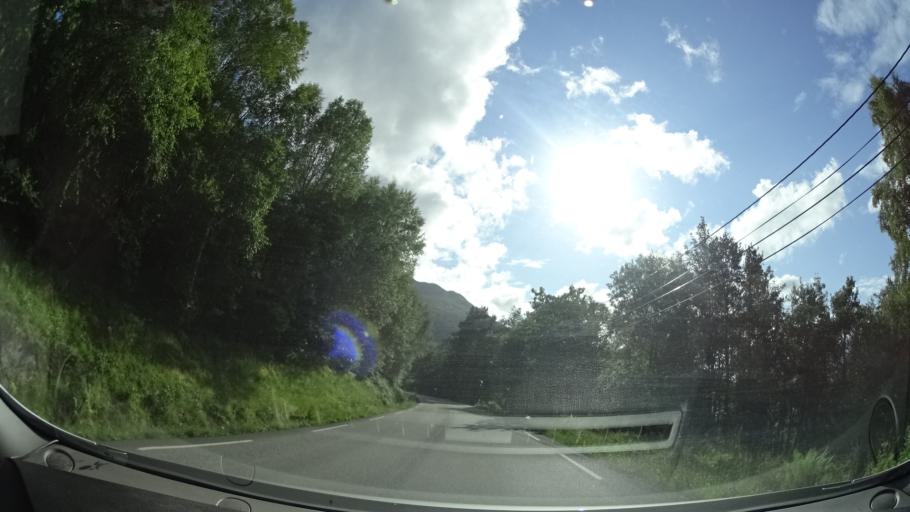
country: NO
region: More og Romsdal
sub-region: Aure
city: Aure
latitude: 63.1363
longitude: 8.4821
